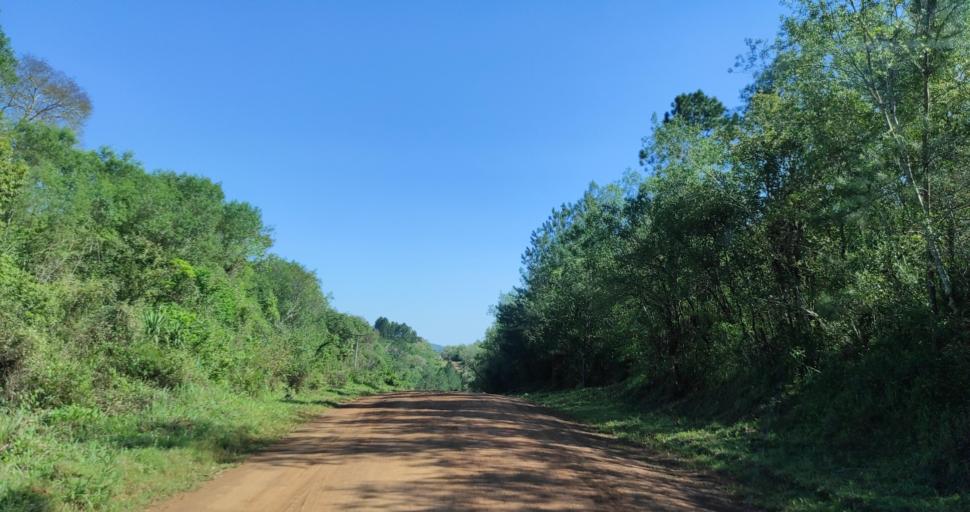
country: AR
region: Misiones
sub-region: Departamento de Candelaria
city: Loreto
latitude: -27.3247
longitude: -55.5280
